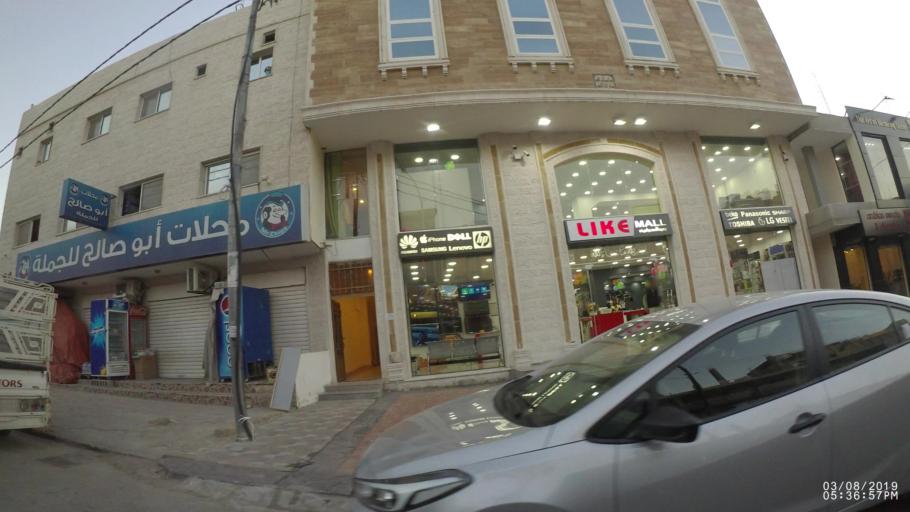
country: JO
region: Ma'an
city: Petra
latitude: 30.3229
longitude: 35.4781
